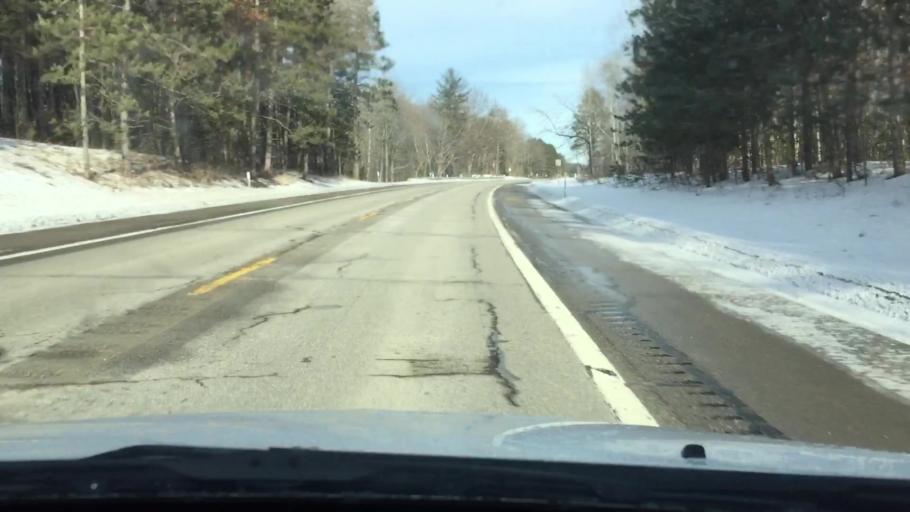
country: US
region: Michigan
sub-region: Kalkaska County
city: Kalkaska
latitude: 44.6068
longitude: -85.3213
